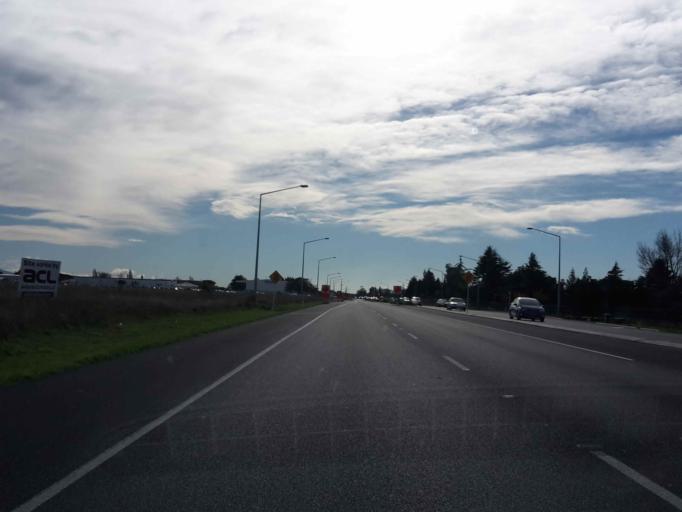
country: NZ
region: Canterbury
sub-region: Selwyn District
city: Prebbleton
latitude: -43.5008
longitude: 172.5452
